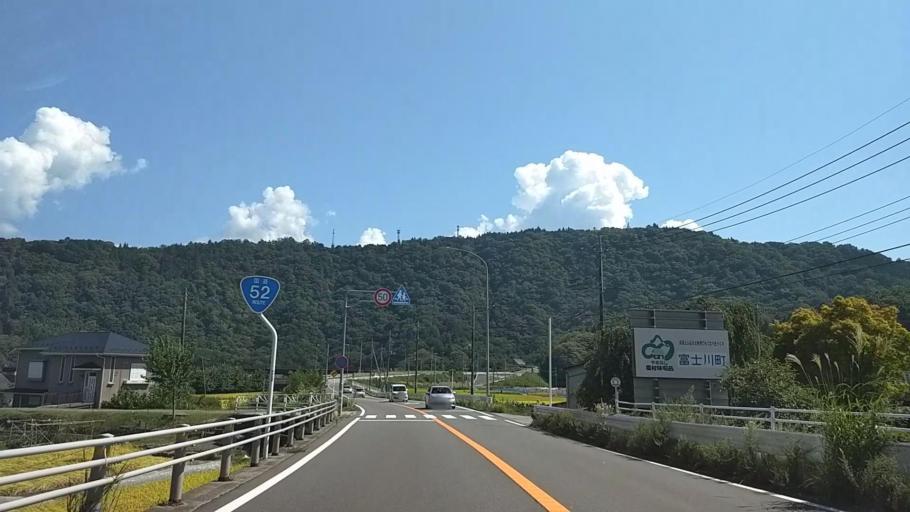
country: JP
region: Yamanashi
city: Ryuo
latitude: 35.5146
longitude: 138.4550
